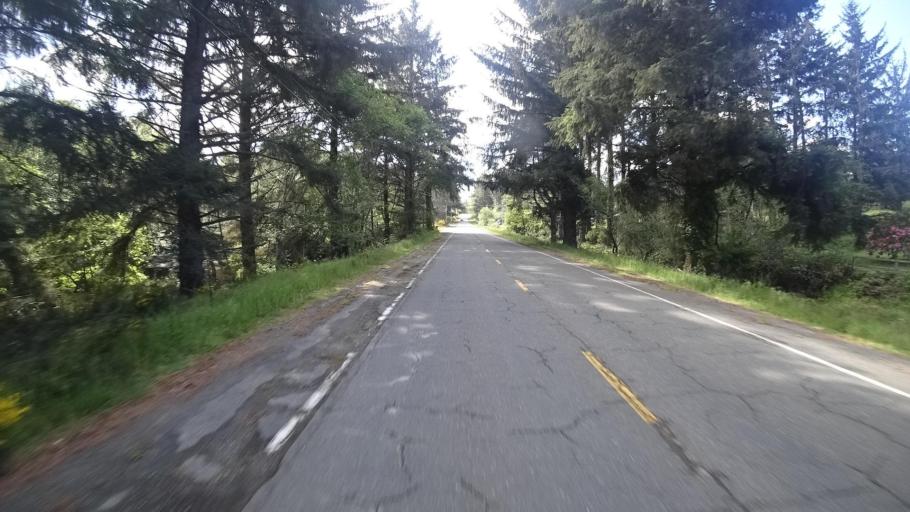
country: US
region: California
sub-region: Humboldt County
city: McKinleyville
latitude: 40.9865
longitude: -124.1072
